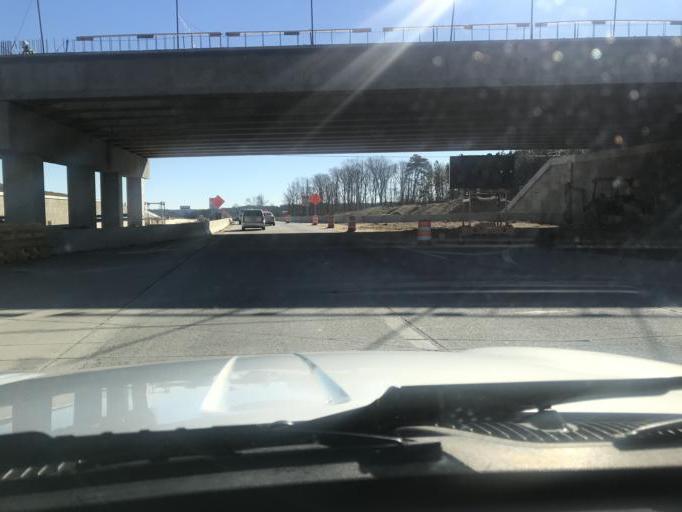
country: US
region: Georgia
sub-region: Barrow County
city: Winder
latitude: 33.9440
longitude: -83.7530
